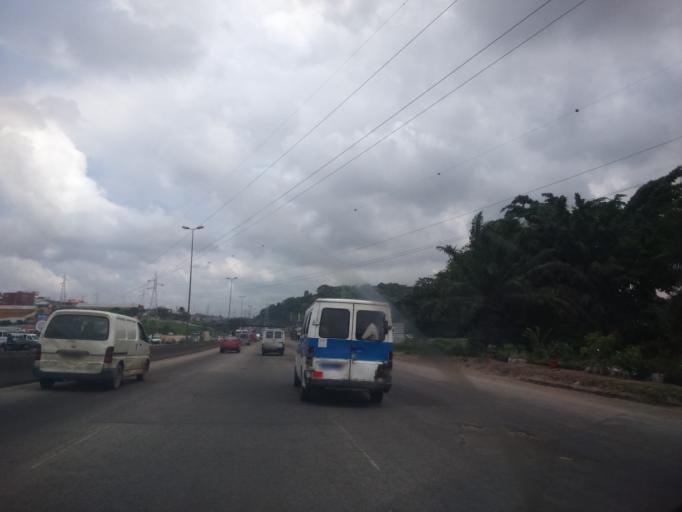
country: CI
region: Lagunes
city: Abidjan
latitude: 5.3600
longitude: -4.0416
